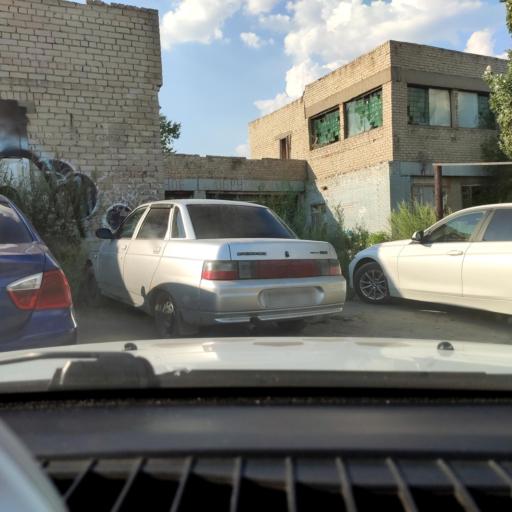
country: RU
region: Perm
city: Perm
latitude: 58.0283
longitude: 56.2390
